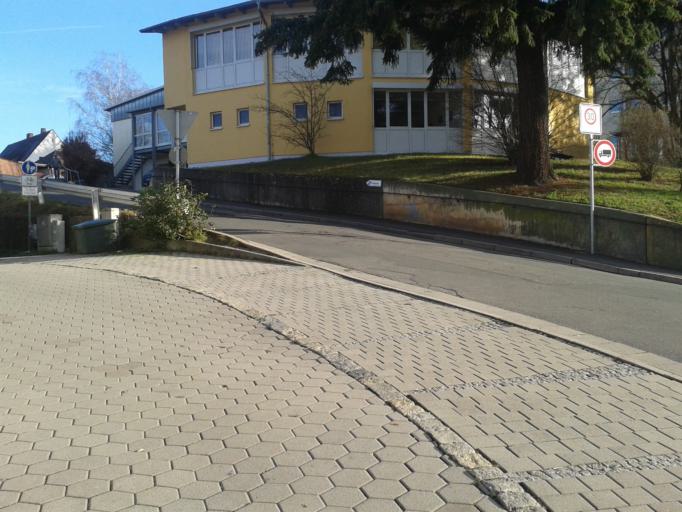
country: DE
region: Bavaria
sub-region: Upper Franconia
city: Kronach
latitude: 50.2359
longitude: 11.3317
